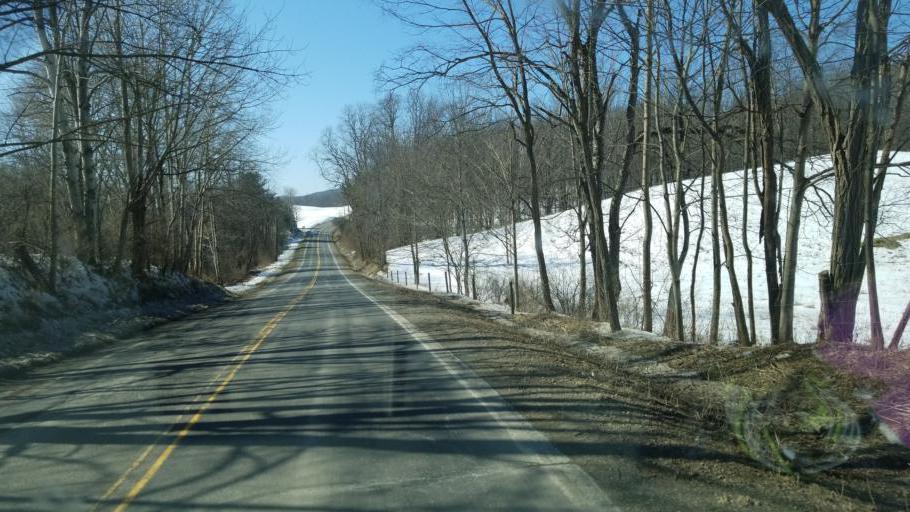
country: US
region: New York
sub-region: Steuben County
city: Hornell
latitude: 42.3574
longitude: -77.7051
